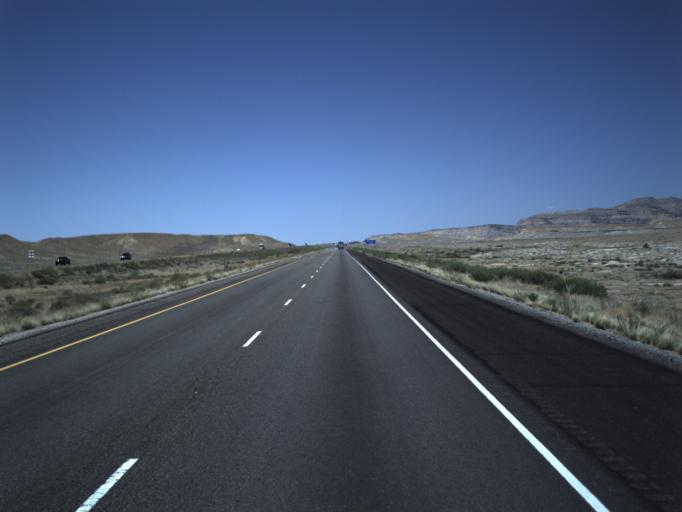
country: US
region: Utah
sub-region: Grand County
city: Moab
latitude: 38.9466
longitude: -109.6559
